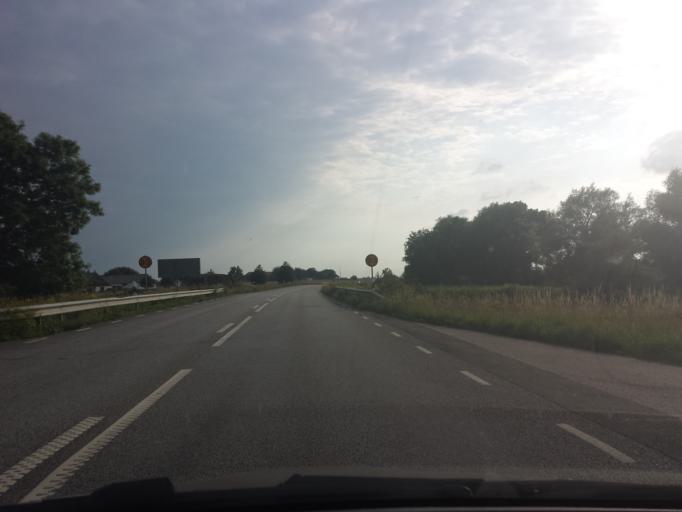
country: SE
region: Skane
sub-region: Ystads Kommun
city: Kopingebro
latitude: 55.4450
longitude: 14.0122
